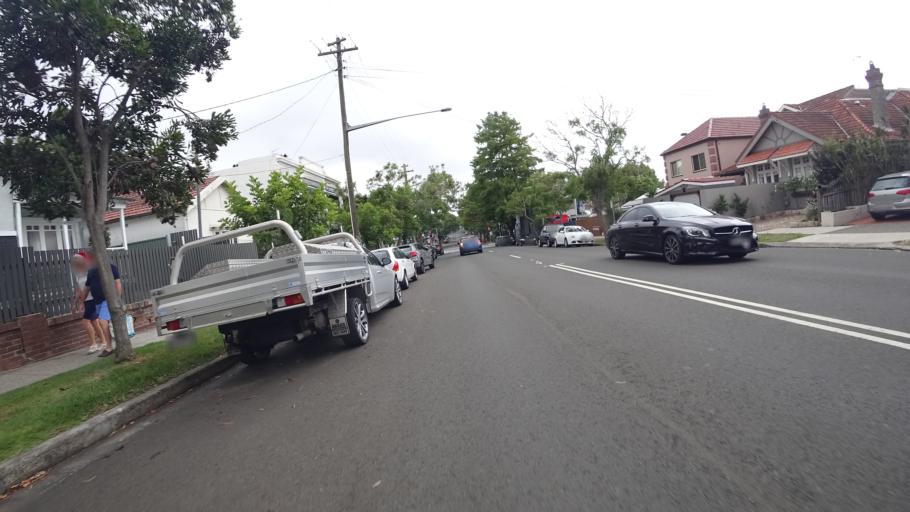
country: AU
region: New South Wales
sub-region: North Sydney
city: Crows Nest
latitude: -33.8293
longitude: 151.2062
